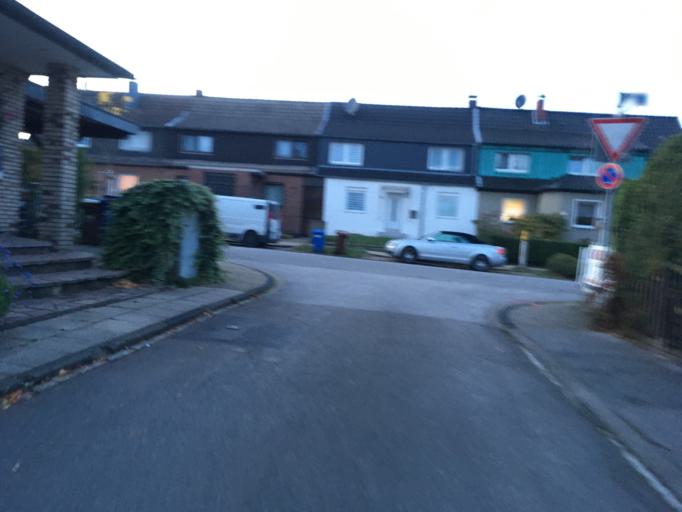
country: DE
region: North Rhine-Westphalia
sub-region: Regierungsbezirk Munster
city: Bottrop
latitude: 51.4765
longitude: 6.9346
